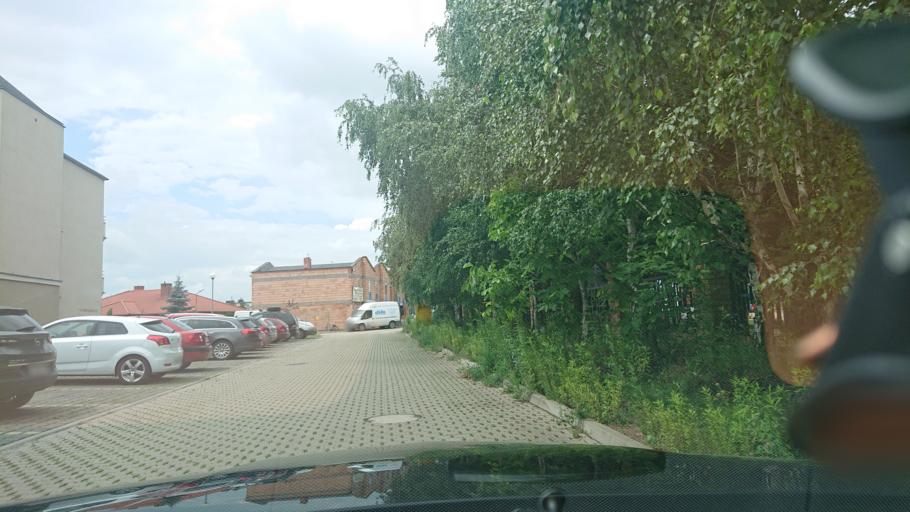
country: PL
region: Greater Poland Voivodeship
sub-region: Powiat gnieznienski
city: Gniezno
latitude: 52.5334
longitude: 17.6304
